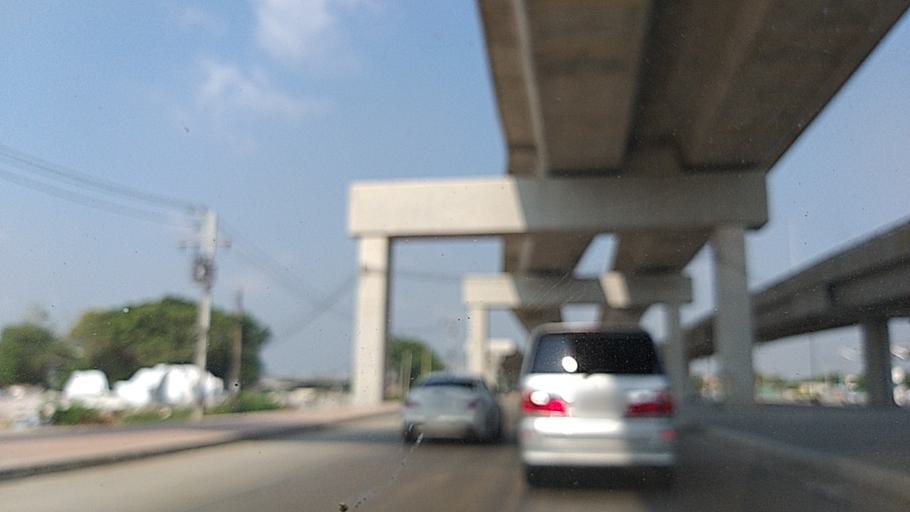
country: TH
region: Bangkok
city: Sai Mai
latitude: 13.9323
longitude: 100.6440
